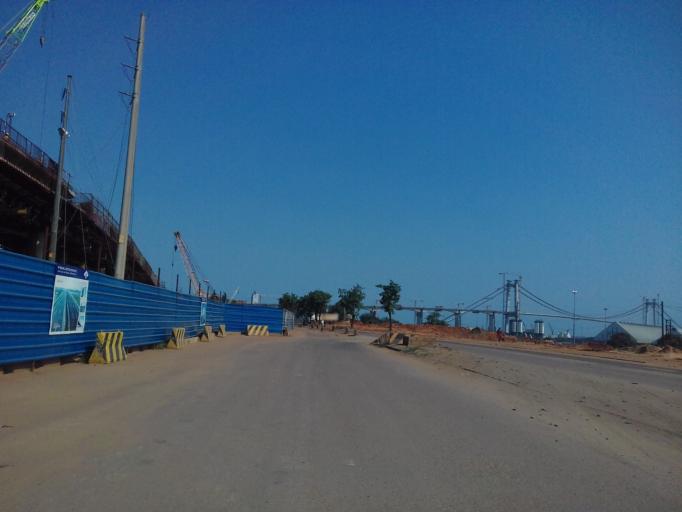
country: MZ
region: Maputo City
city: Maputo
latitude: -25.9561
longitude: 32.5528
